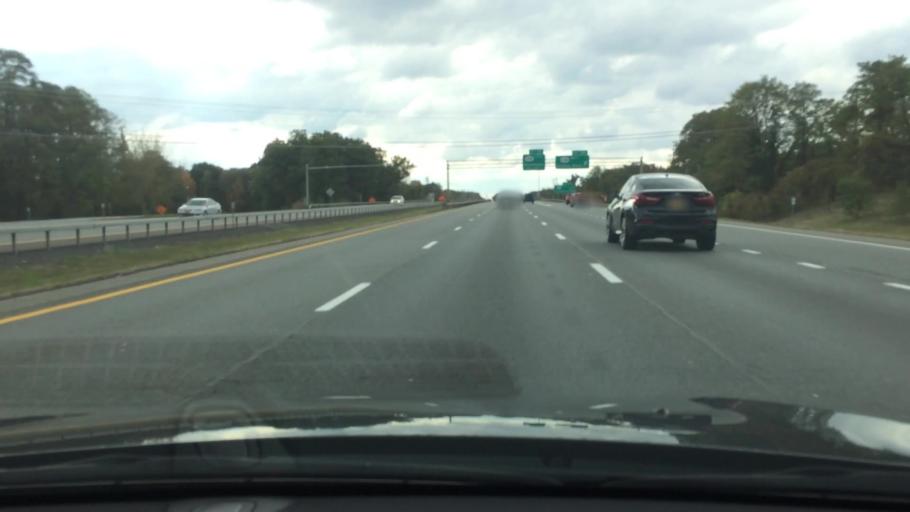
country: US
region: New York
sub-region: Saratoga County
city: Country Knolls
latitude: 42.8654
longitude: -73.7759
